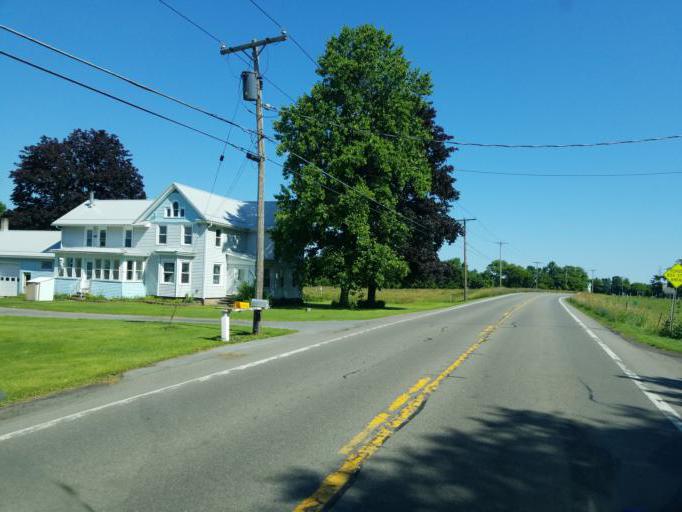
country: US
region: New York
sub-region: Wayne County
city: Clyde
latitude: 43.1051
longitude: -76.8700
